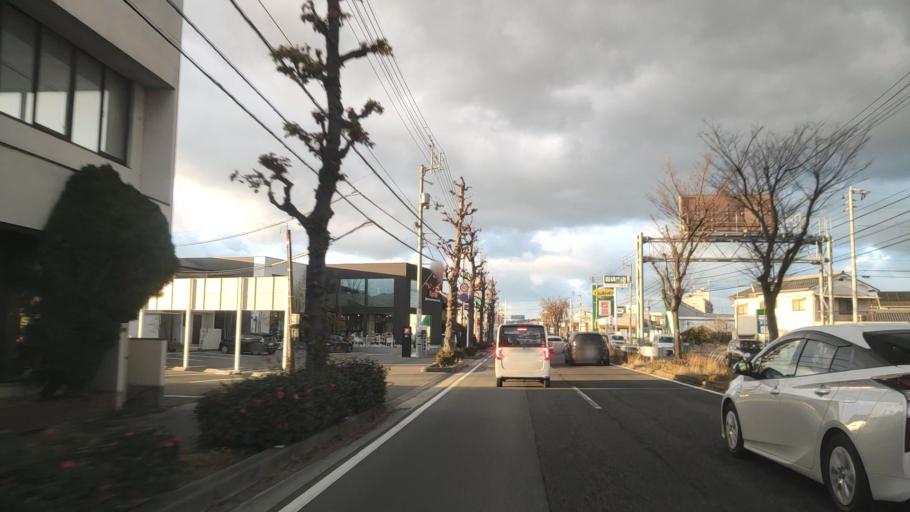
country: JP
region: Ehime
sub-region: Shikoku-chuo Shi
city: Matsuyama
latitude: 33.8074
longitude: 132.7810
